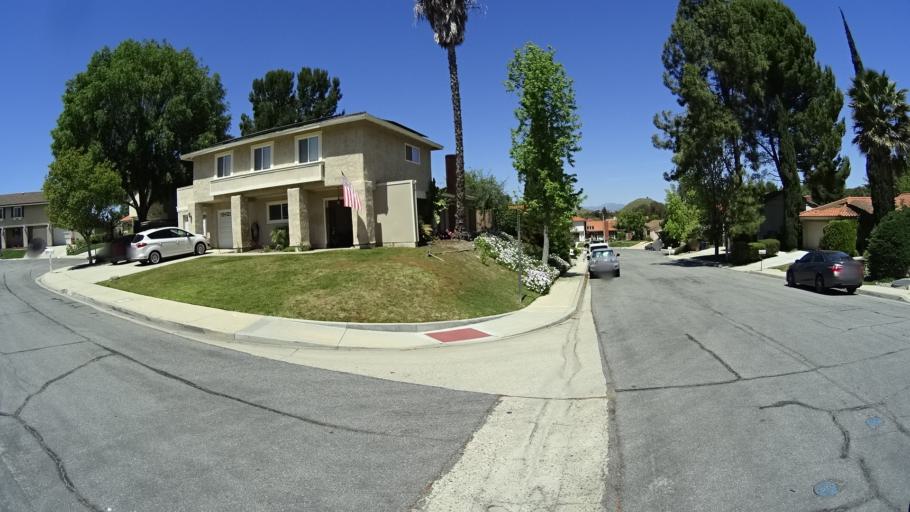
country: US
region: California
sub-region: Ventura County
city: Casa Conejo
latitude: 34.1767
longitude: -118.8908
